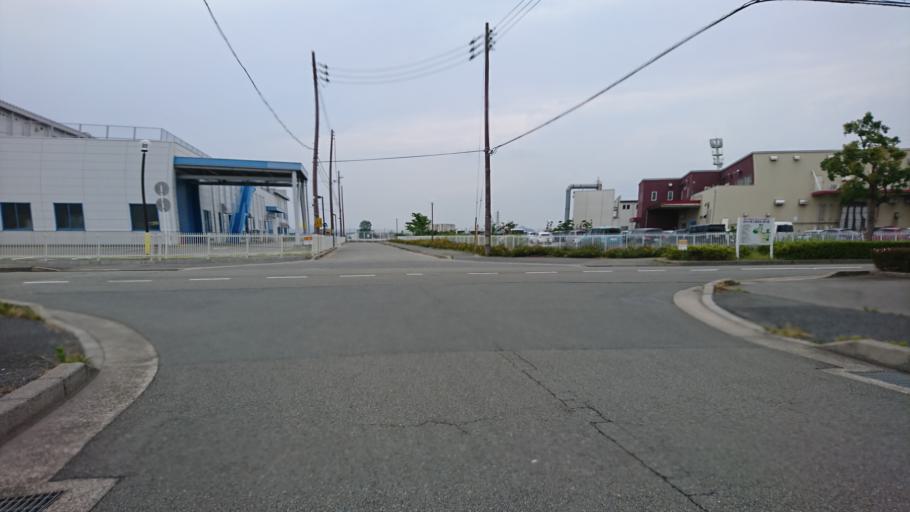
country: JP
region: Hyogo
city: Kakogawacho-honmachi
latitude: 34.7356
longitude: 134.8848
